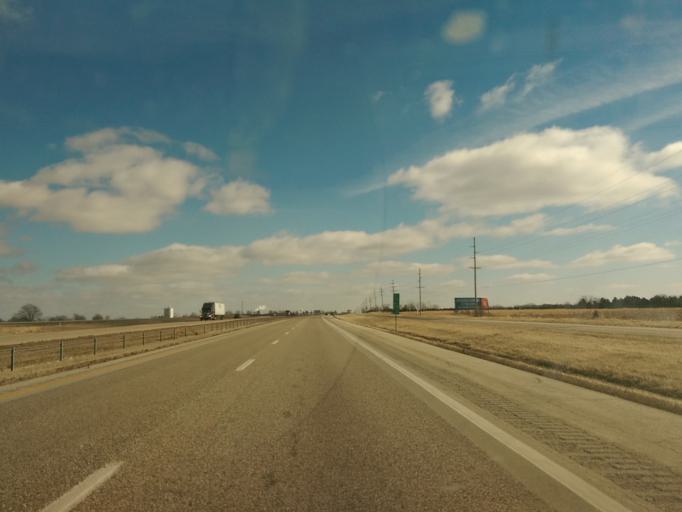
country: US
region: Missouri
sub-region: Montgomery County
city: Montgomery City
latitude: 38.8854
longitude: -91.4066
